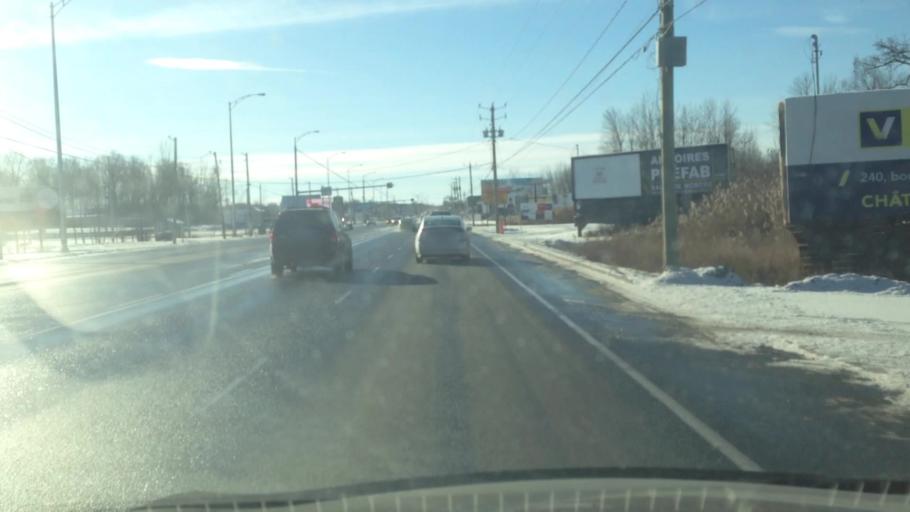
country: CA
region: Quebec
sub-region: Monteregie
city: Chateauguay
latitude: 45.3735
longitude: -73.7073
